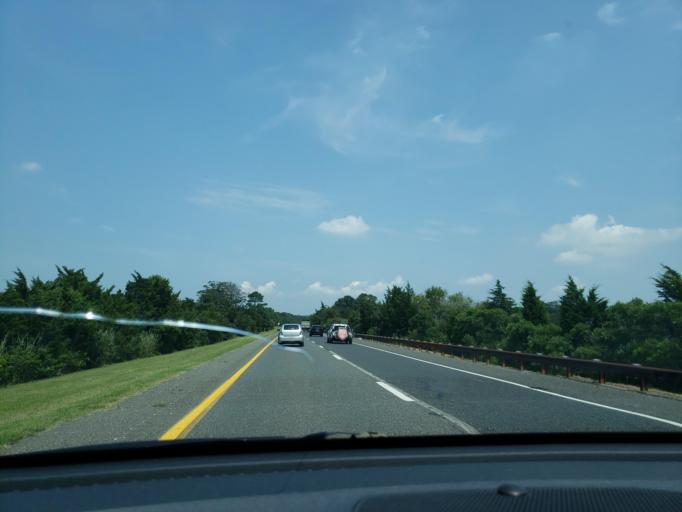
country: US
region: New Jersey
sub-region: Cape May County
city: Erma
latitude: 38.9676
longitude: -74.8985
